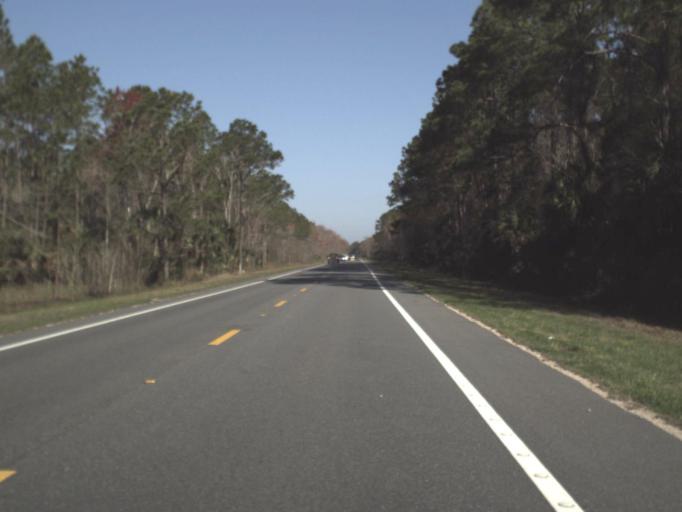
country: US
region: Florida
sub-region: Leon County
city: Woodville
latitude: 30.1670
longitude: -84.0057
